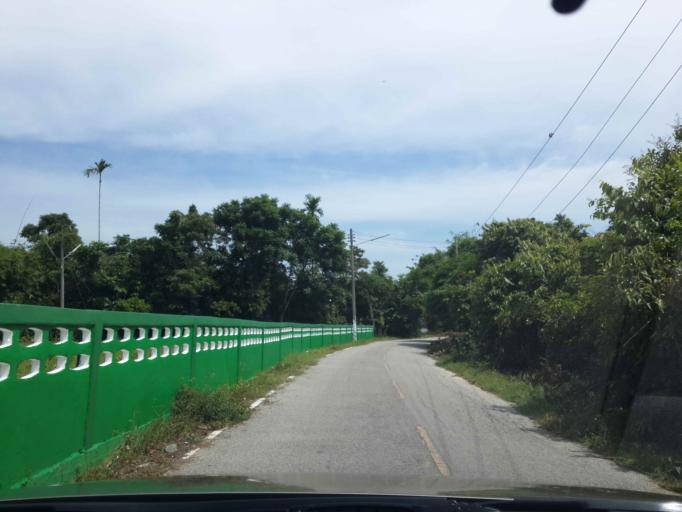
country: TH
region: Narathiwat
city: Rueso
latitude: 6.4011
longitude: 101.5161
